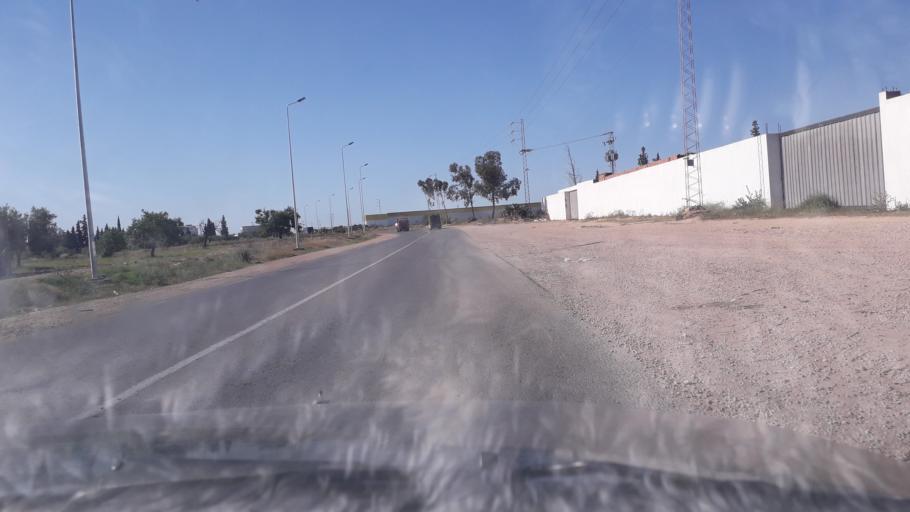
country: TN
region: Safaqis
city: Al Qarmadah
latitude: 34.8730
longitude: 10.7559
